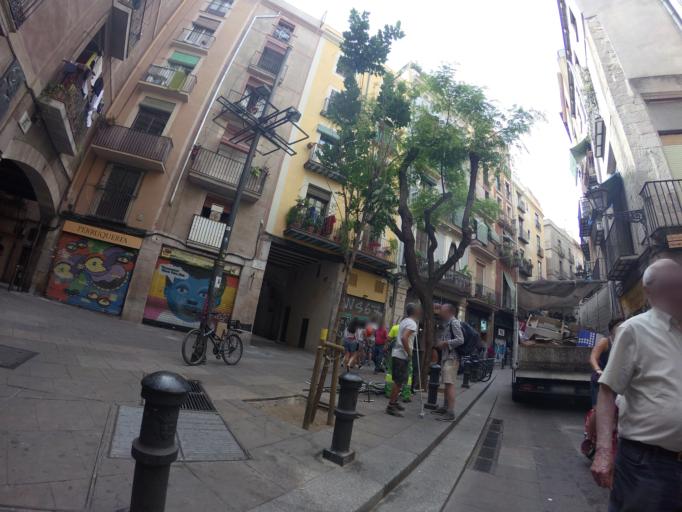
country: ES
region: Catalonia
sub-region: Provincia de Barcelona
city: Ciutat Vella
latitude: 41.3858
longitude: 2.1799
